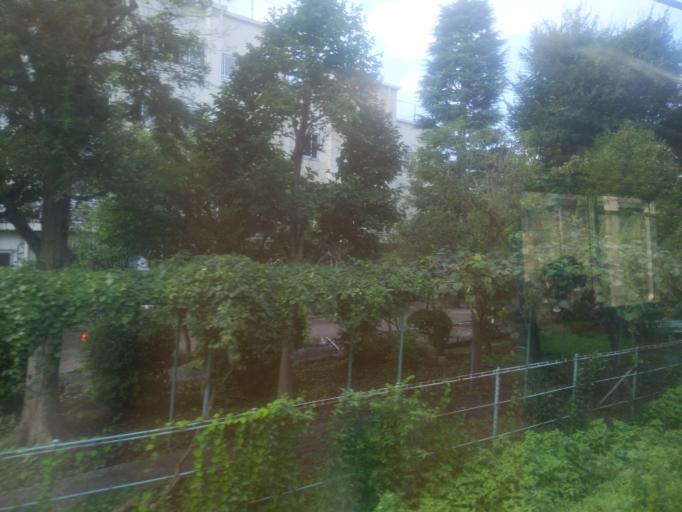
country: JP
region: Tokyo
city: Tokyo
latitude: 35.7156
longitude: 139.6784
